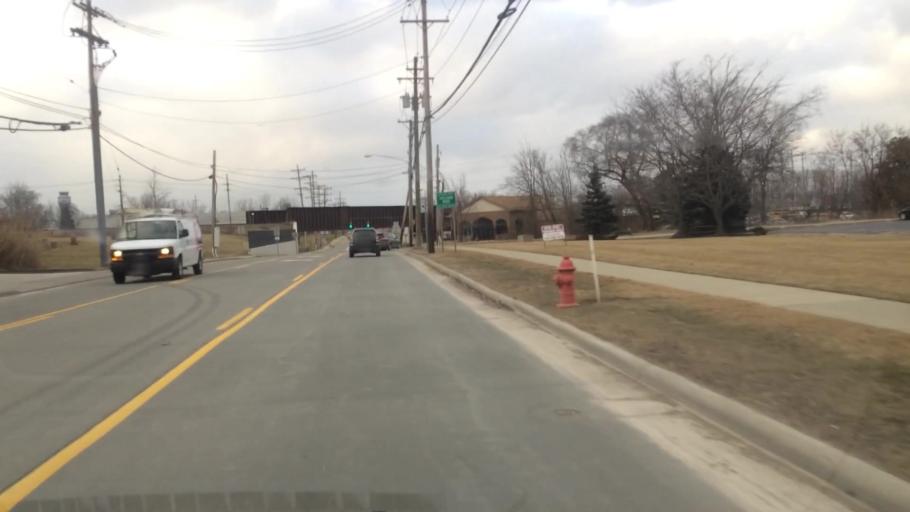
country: US
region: Ohio
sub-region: Cuyahoga County
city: Berea
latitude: 41.3877
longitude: -81.8429
